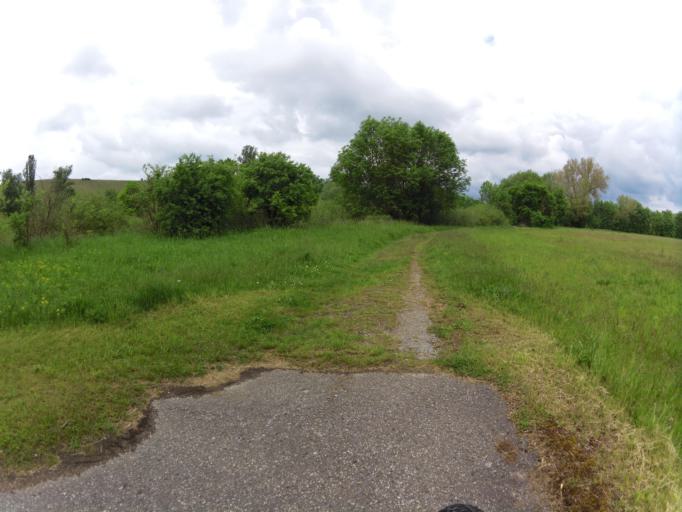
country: DE
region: Bavaria
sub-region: Regierungsbezirk Unterfranken
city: Sommerach
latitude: 49.8296
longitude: 10.1923
